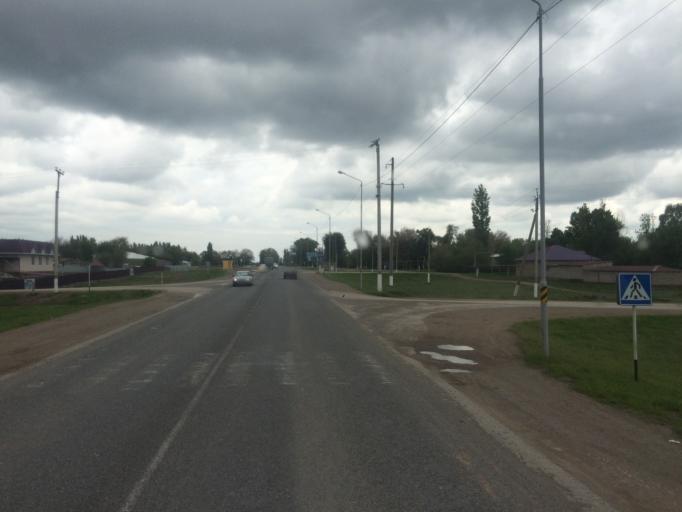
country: KZ
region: Zhambyl
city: Georgiyevka
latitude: 43.1436
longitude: 74.6154
